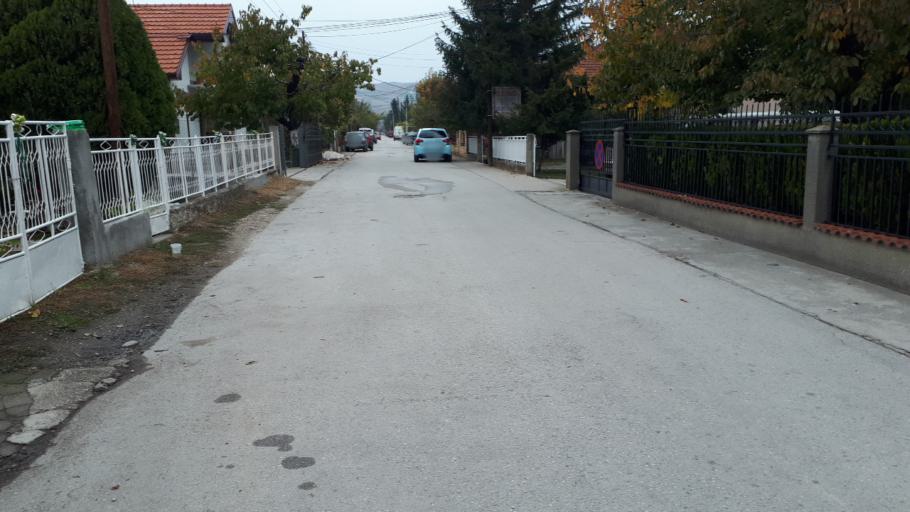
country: MK
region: Saraj
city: Saraj
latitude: 42.0210
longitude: 21.3570
